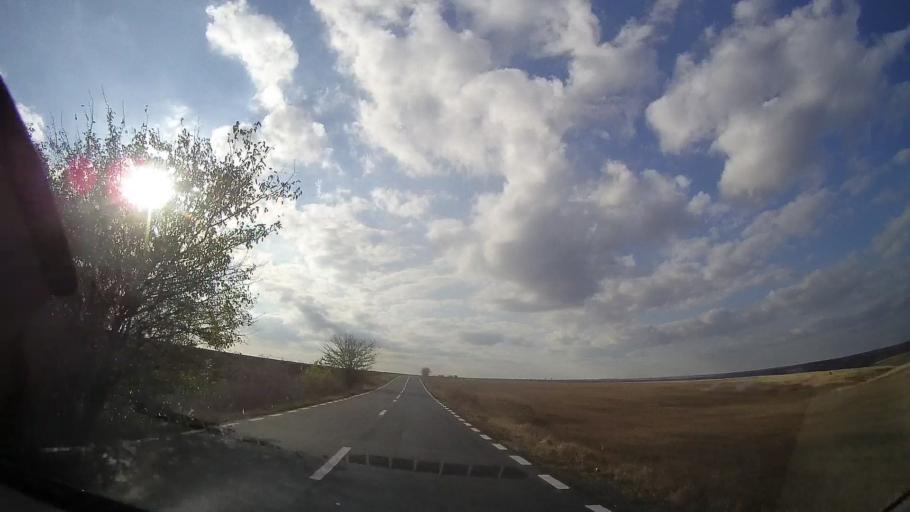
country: RO
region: Constanta
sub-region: Comuna Albesti
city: Albesti
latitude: 43.8090
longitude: 28.4063
